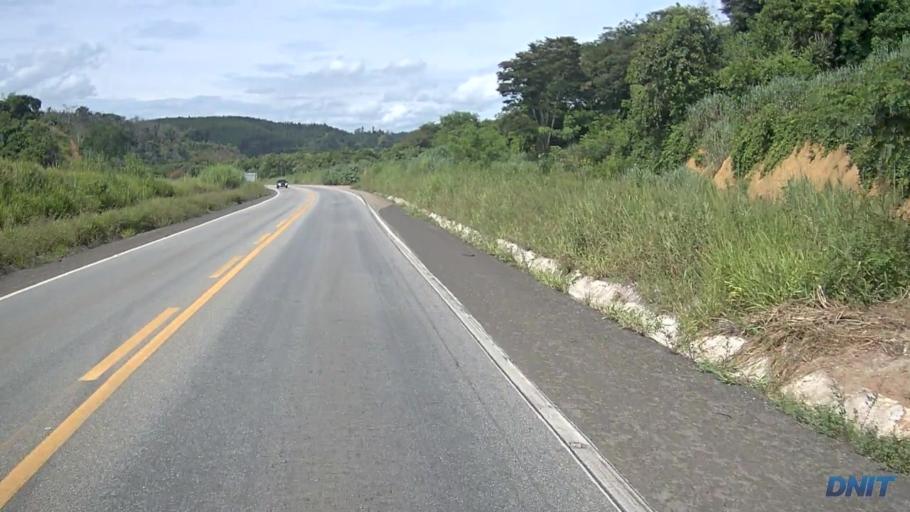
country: BR
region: Minas Gerais
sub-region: Ipaba
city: Ipaba
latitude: -19.3905
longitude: -42.4786
